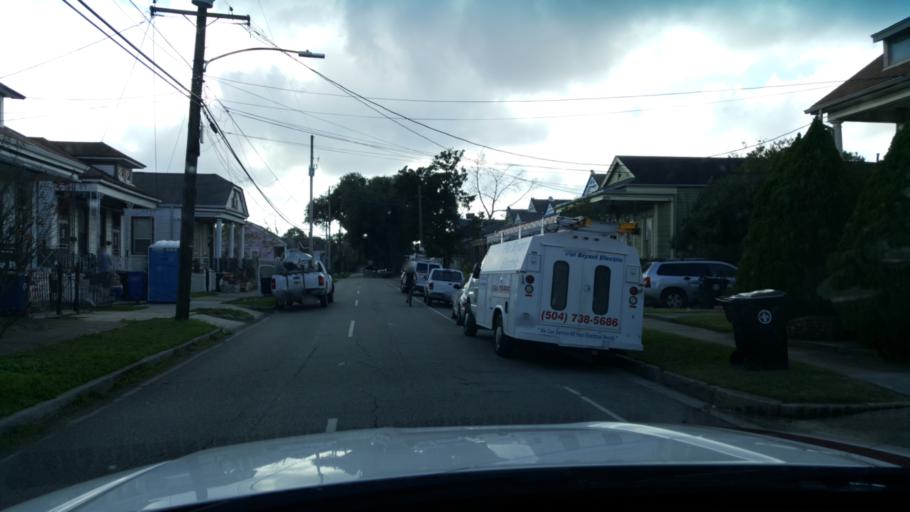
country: US
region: Louisiana
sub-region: Orleans Parish
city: New Orleans
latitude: 29.9755
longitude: -90.0717
